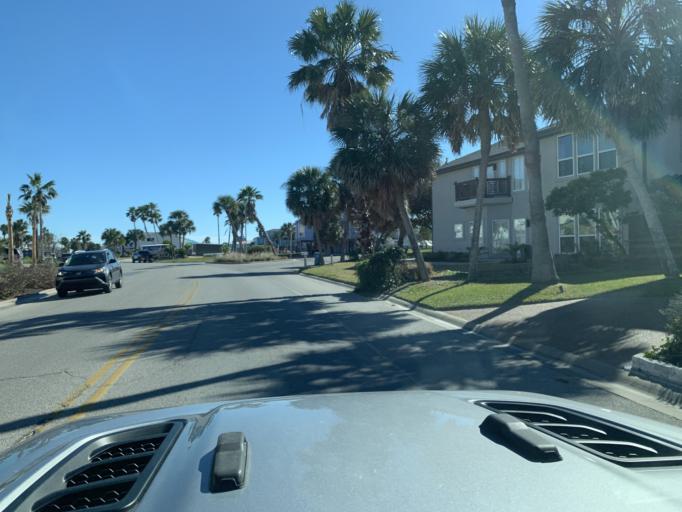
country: US
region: Texas
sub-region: Aransas County
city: Fulton
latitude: 28.0423
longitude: -97.0269
